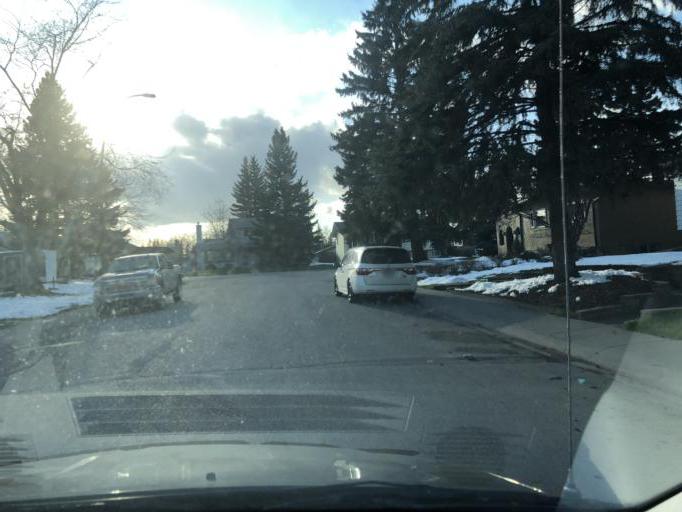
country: CA
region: Alberta
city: Calgary
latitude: 50.9422
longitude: -114.0406
